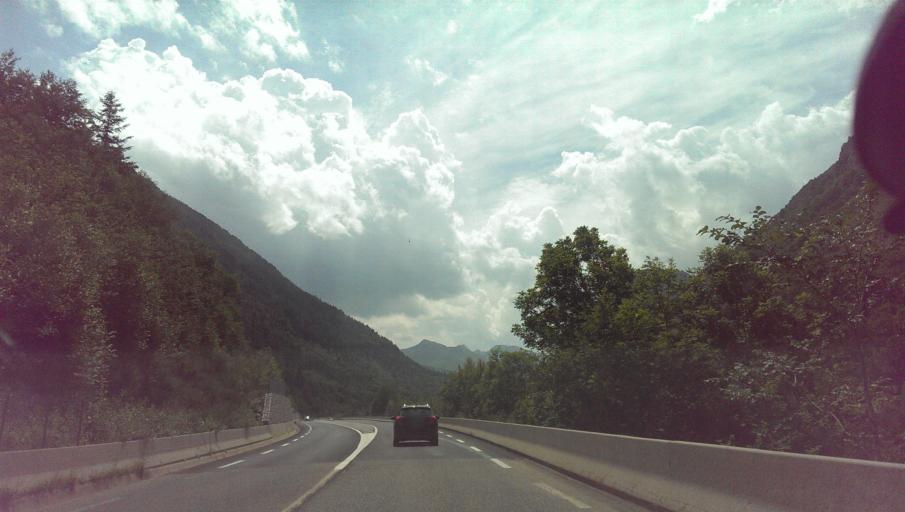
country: AD
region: Encamp
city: Pas de la Casa
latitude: 42.6038
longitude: 1.8128
